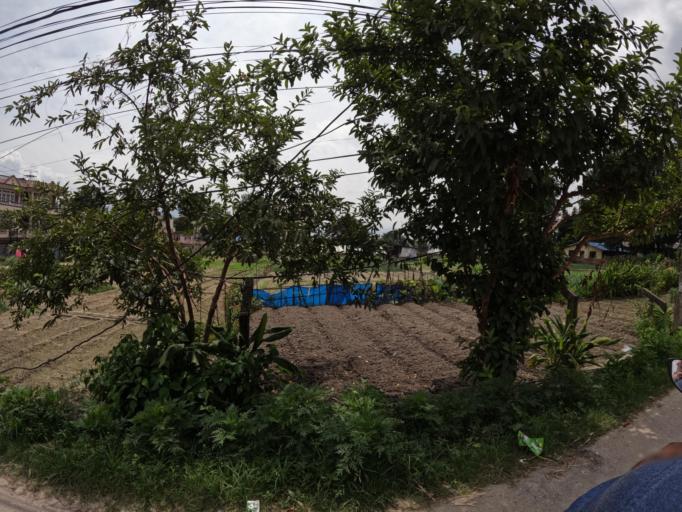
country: NP
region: Central Region
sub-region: Bagmati Zone
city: Bhaktapur
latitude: 27.6828
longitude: 85.3796
